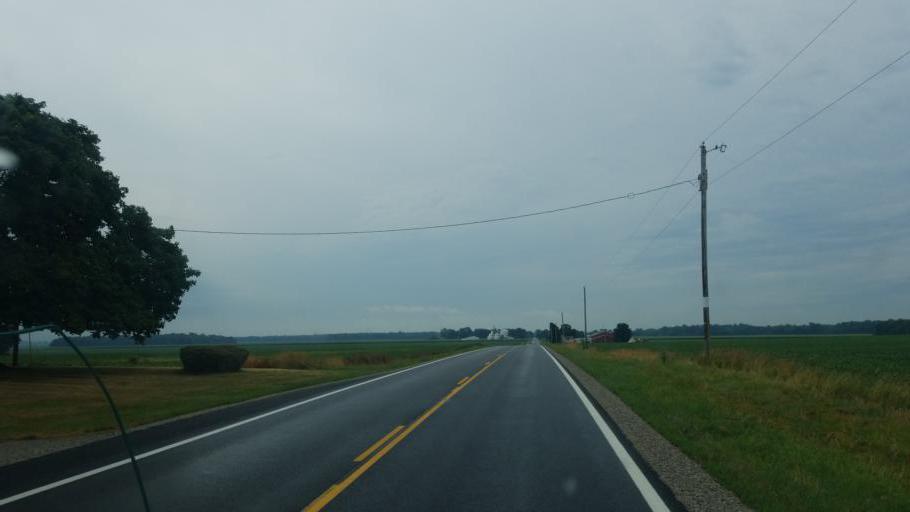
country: US
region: Ohio
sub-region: Williams County
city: Edgerton
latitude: 41.3770
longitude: -84.6697
